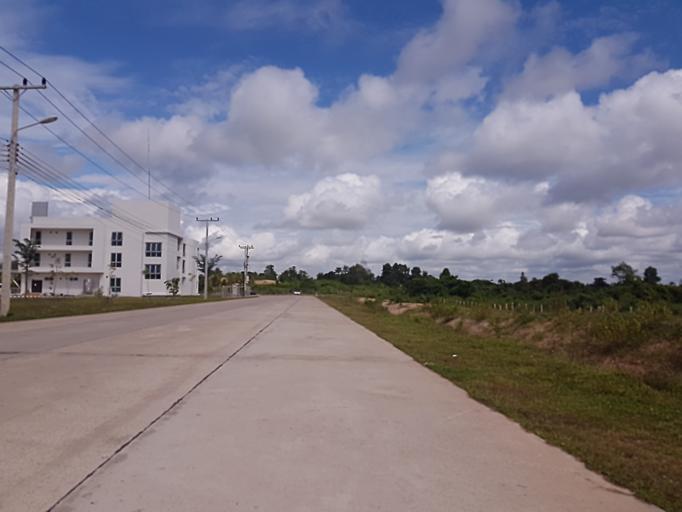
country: TH
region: Nong Khai
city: Nong Khai
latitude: 17.9178
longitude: 102.7074
